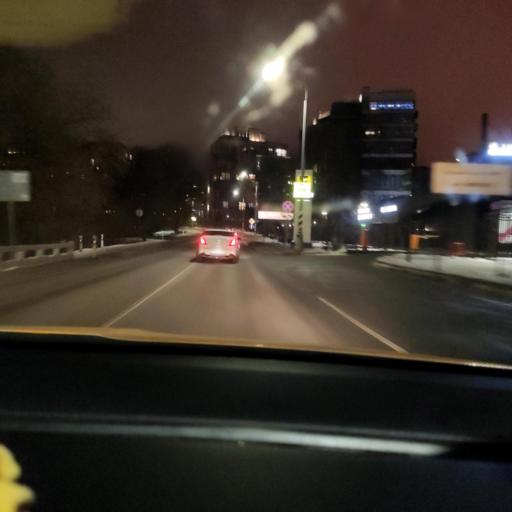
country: RU
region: Moscow
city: Khimki
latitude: 55.8918
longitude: 37.3749
